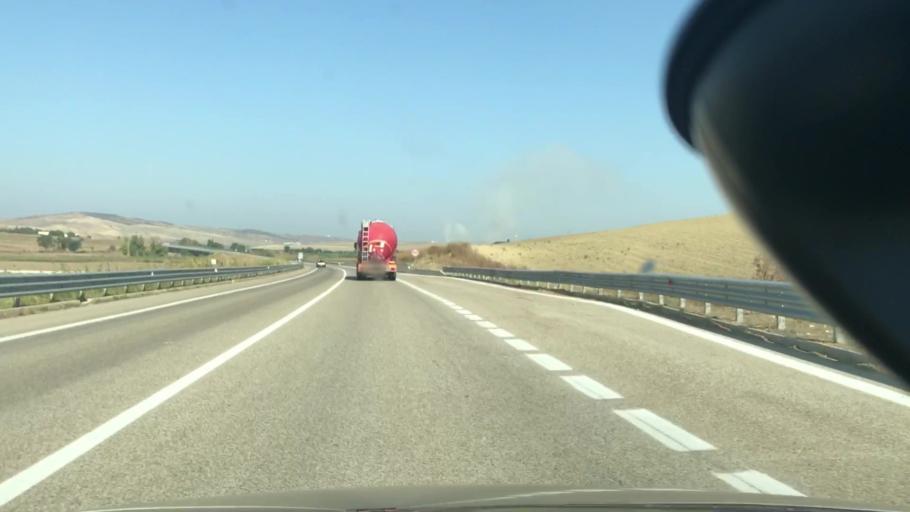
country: IT
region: Basilicate
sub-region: Provincia di Matera
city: Irsina
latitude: 40.7791
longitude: 16.3170
